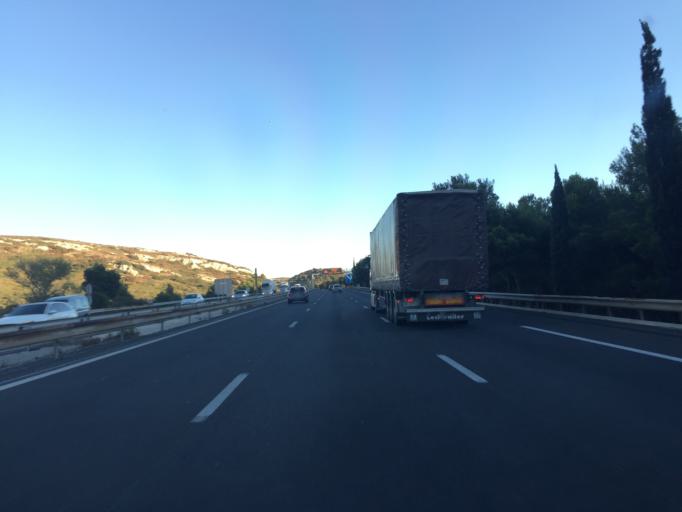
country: FR
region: Provence-Alpes-Cote d'Azur
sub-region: Departement des Bouches-du-Rhone
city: La Fare-les-Oliviers
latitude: 43.5762
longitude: 5.2115
